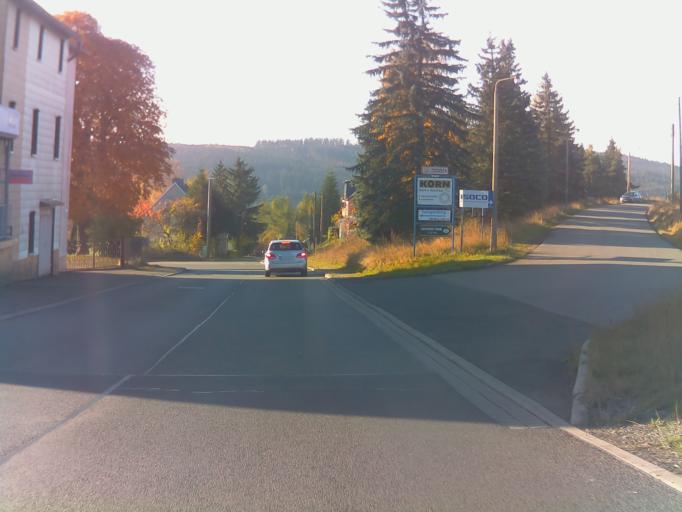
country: DE
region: Thuringia
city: Schmiedefeld
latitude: 50.5322
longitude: 11.2150
